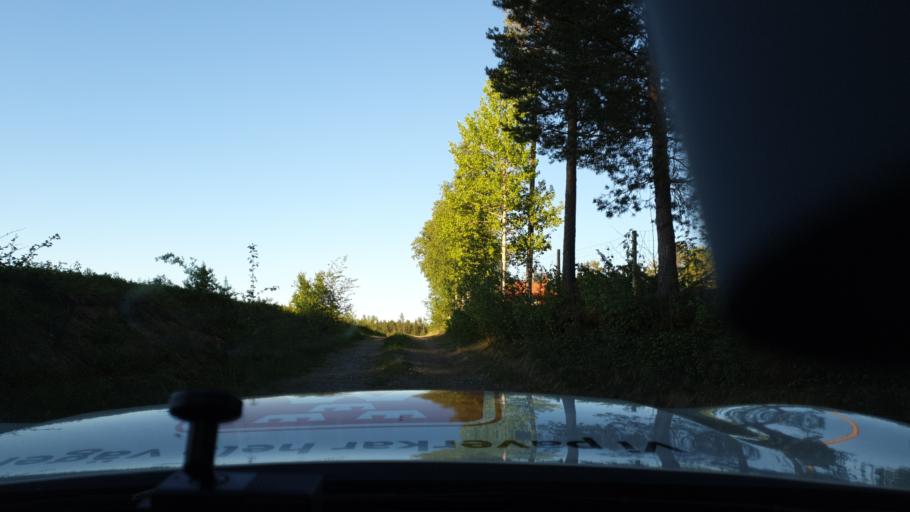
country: SE
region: Vaesterbotten
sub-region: Vannas Kommun
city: Vannasby
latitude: 64.0084
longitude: 20.0496
